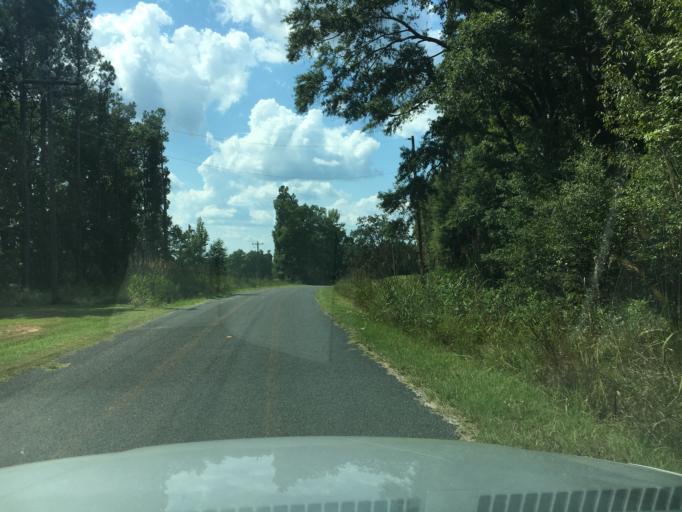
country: US
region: South Carolina
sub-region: Greenwood County
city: Greenwood
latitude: 34.0627
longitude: -82.1485
